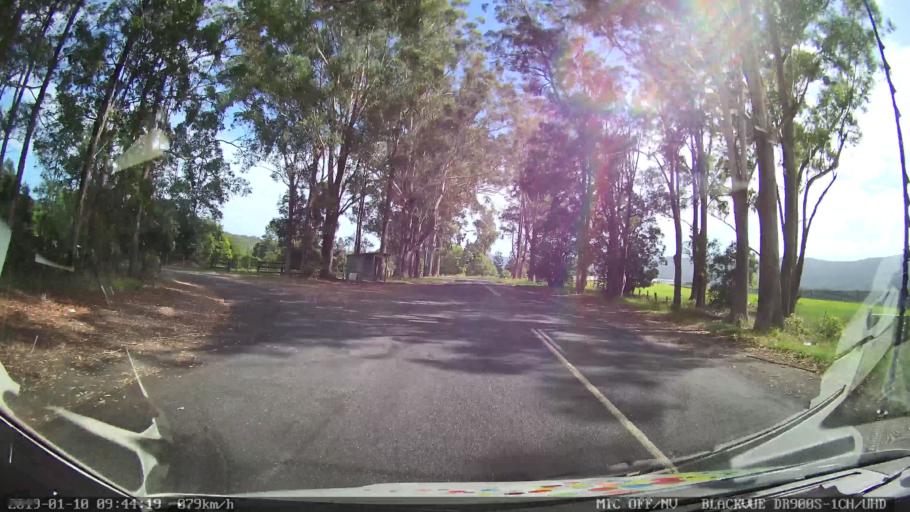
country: AU
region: New South Wales
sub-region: Coffs Harbour
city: Nana Glen
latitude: -30.1182
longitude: 153.0036
